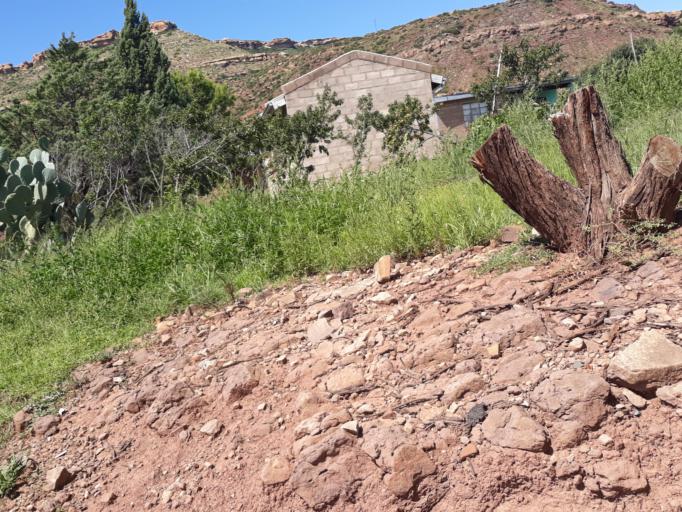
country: LS
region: Quthing
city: Quthing
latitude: -30.3328
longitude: 27.5346
